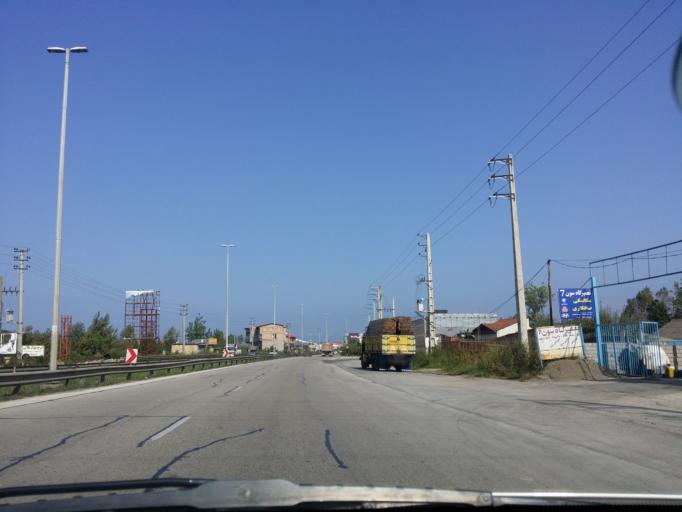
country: IR
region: Mazandaran
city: Chalus
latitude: 36.6727
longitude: 51.3954
